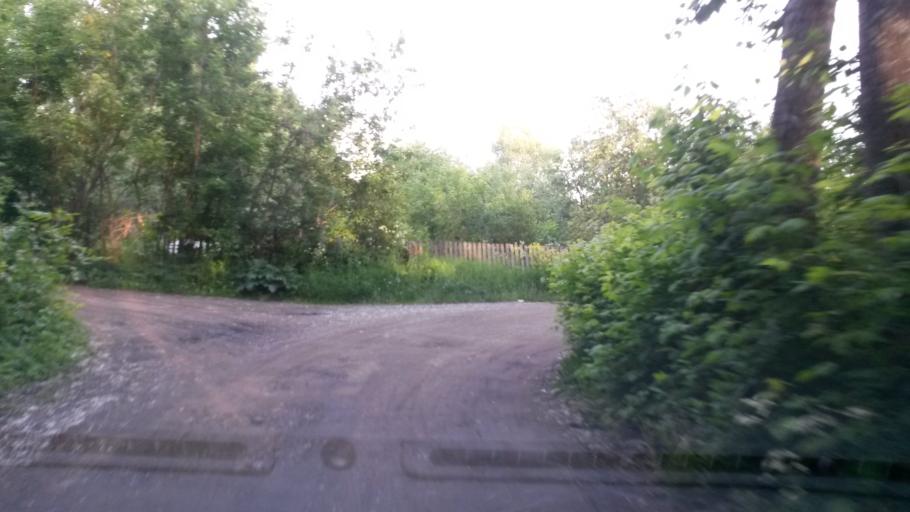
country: RU
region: Jaroslavl
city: Yaroslavl
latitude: 57.7003
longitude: 39.8237
